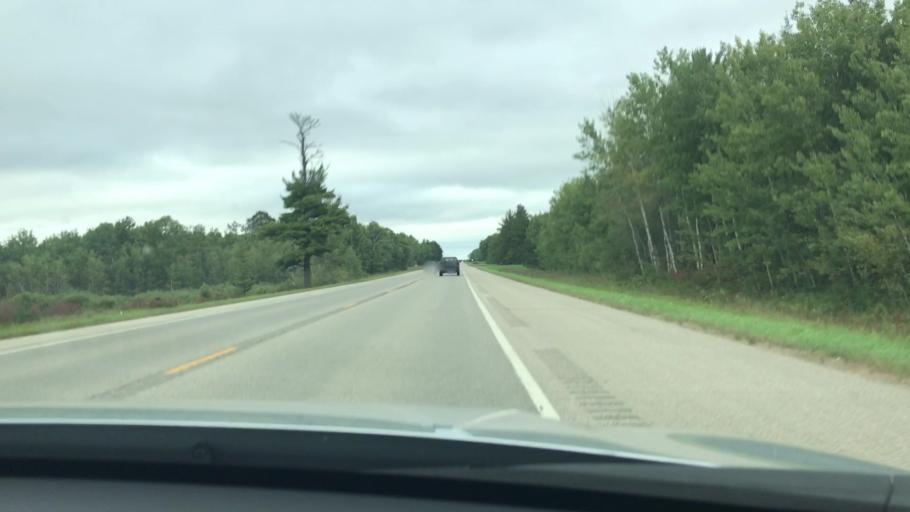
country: US
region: Minnesota
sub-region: Hubbard County
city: Park Rapids
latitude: 46.8425
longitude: -95.0842
